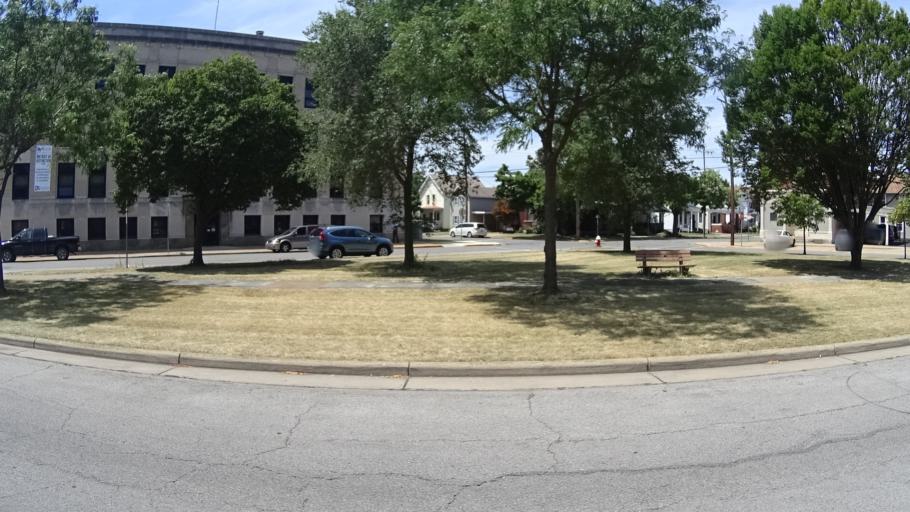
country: US
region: Ohio
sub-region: Erie County
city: Sandusky
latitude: 41.4523
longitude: -82.7130
